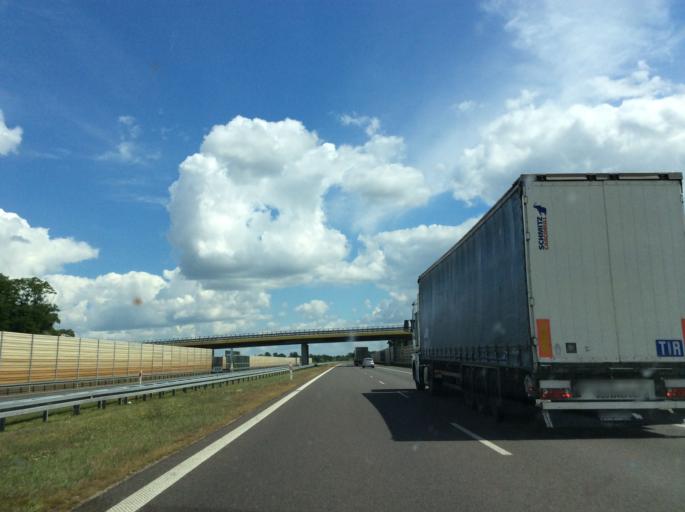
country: PL
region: Greater Poland Voivodeship
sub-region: Powiat turecki
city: Brudzew
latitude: 52.1301
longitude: 18.6560
